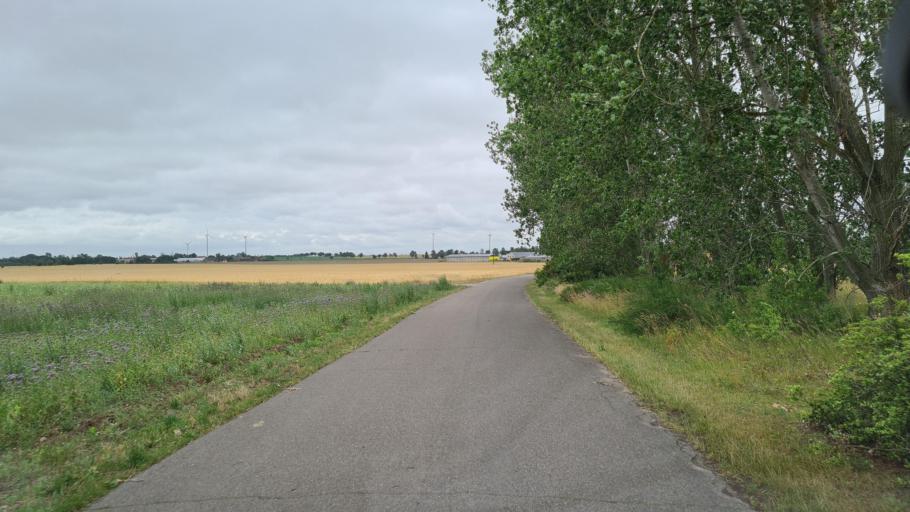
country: DE
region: Brandenburg
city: Juterbog
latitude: 51.9420
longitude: 13.1907
